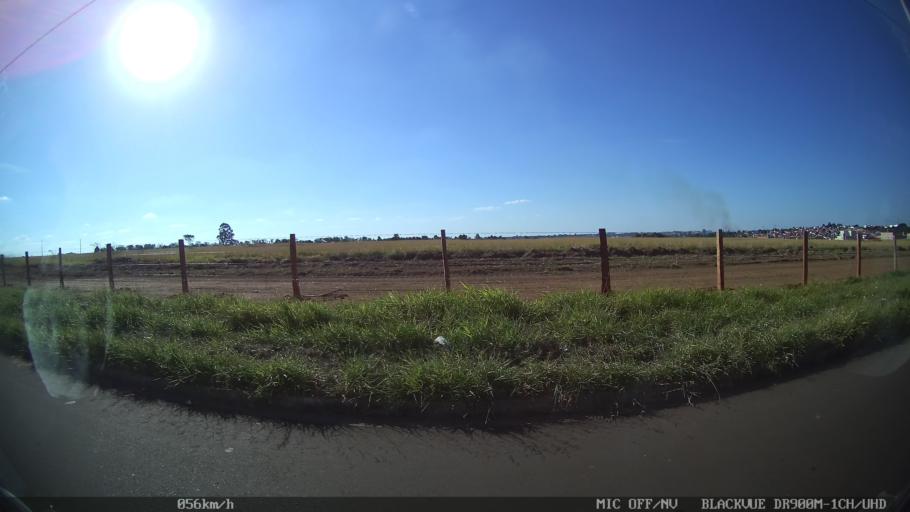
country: BR
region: Sao Paulo
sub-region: Franca
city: Franca
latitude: -20.5061
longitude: -47.4318
